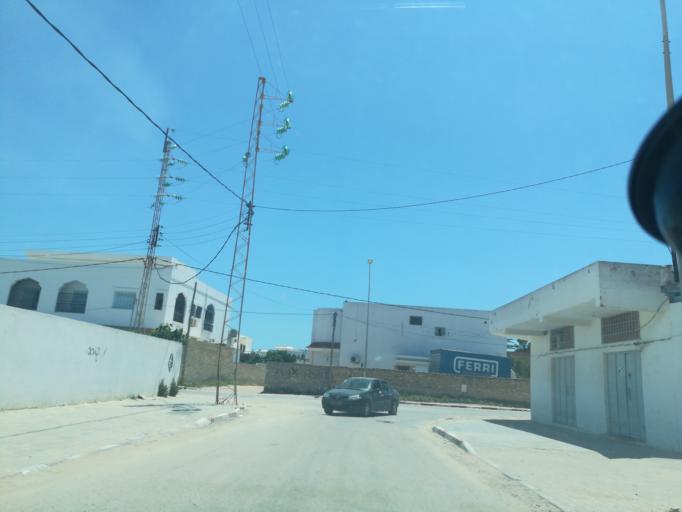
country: TN
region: Safaqis
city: Al Qarmadah
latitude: 34.8184
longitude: 10.7594
